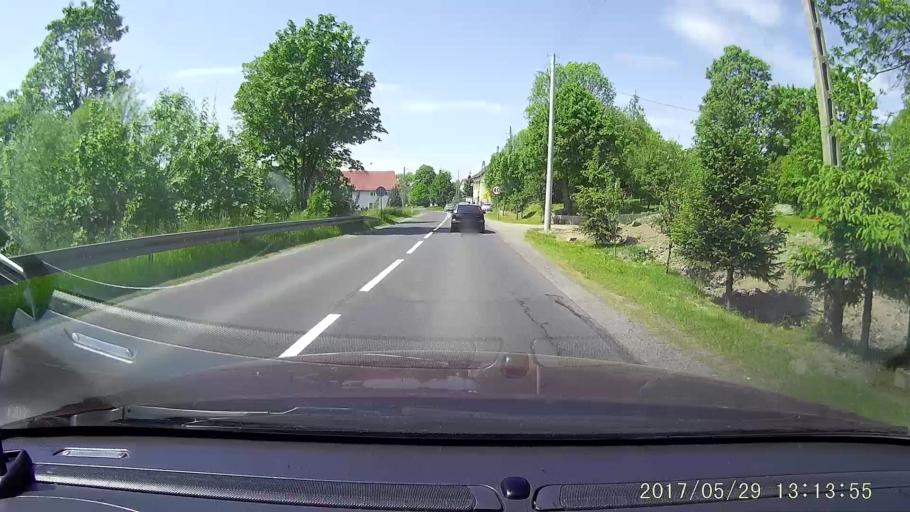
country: PL
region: Lower Silesian Voivodeship
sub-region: Powiat lwowecki
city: Lubomierz
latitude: 50.9774
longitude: 15.4942
